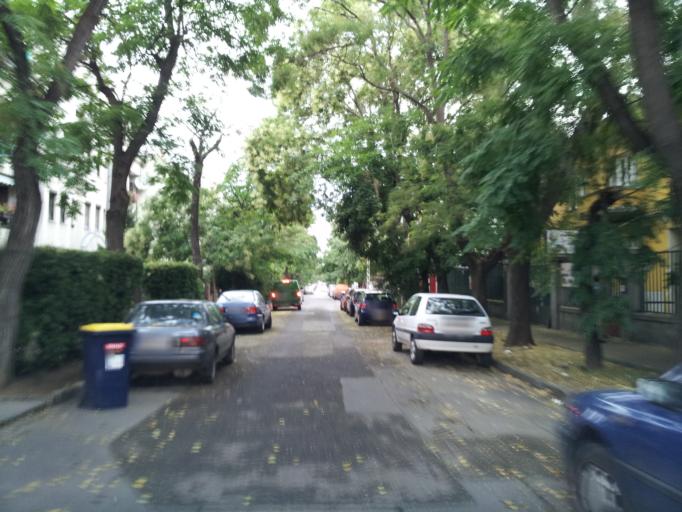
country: HU
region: Budapest
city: Budapest XIV. keruelet
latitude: 47.5171
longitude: 19.1178
